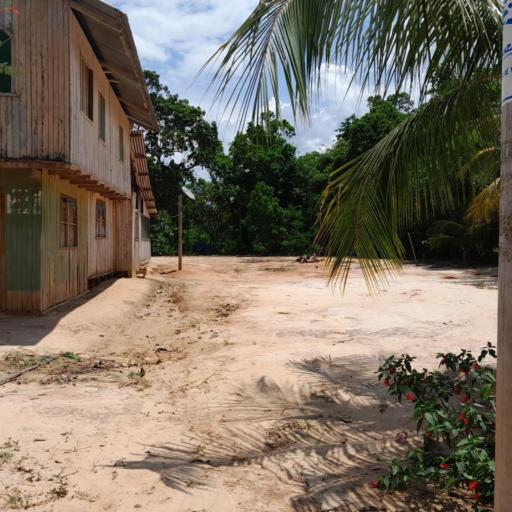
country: PE
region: Ucayali
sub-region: Provincia de Coronel Portillo
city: Puerto Callao
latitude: -8.2710
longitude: -74.6494
